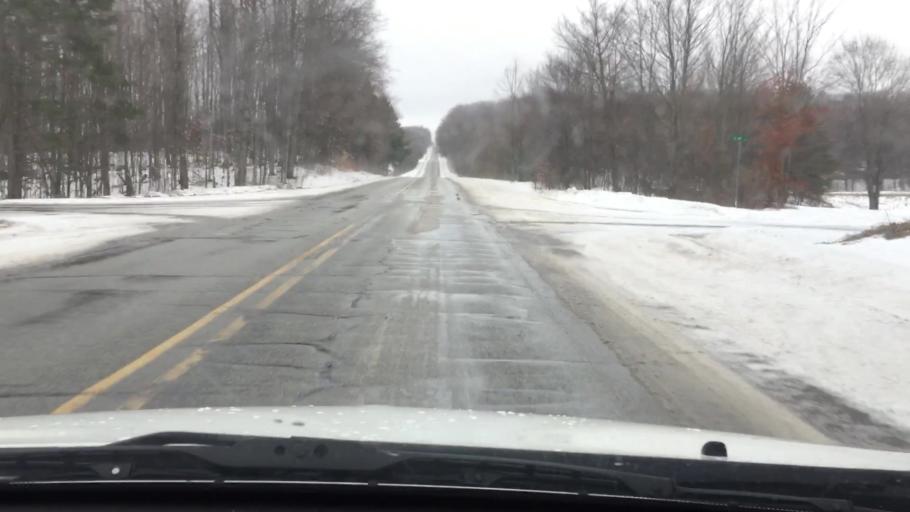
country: US
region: Michigan
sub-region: Wexford County
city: Cadillac
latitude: 44.1941
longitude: -85.4057
